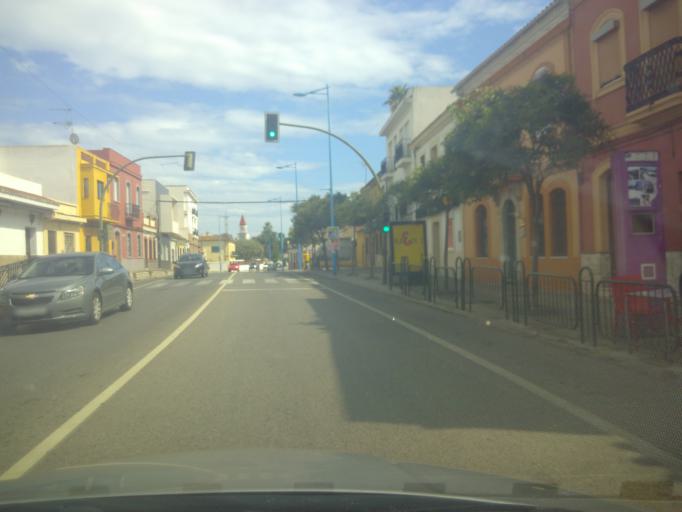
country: ES
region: Andalusia
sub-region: Provincia de Cadiz
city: La Linea de la Concepcion
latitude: 36.1780
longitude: -5.3776
